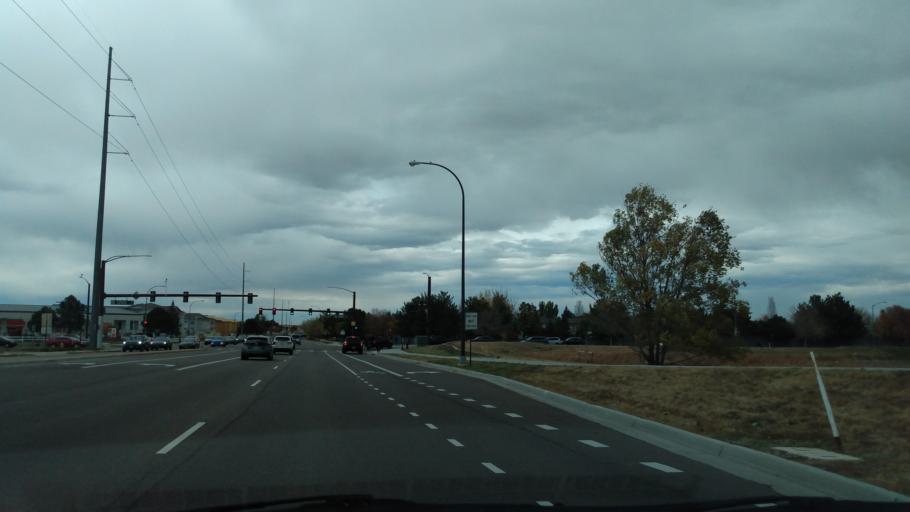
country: US
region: Colorado
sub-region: Adams County
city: Northglenn
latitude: 39.9275
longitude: -104.9778
